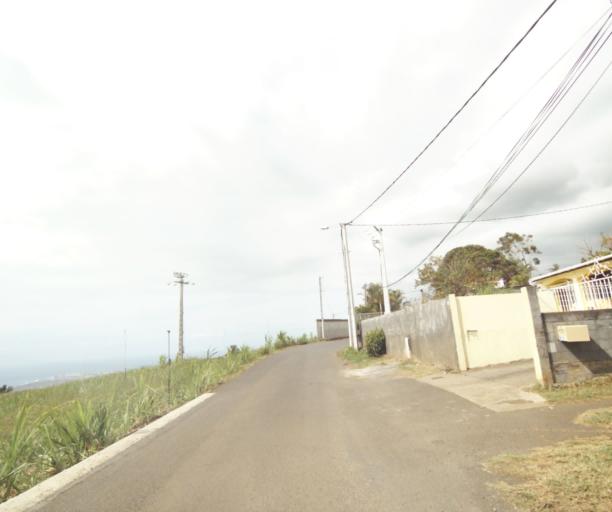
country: RE
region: Reunion
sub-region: Reunion
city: Saint-Paul
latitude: -21.0336
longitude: 55.2903
